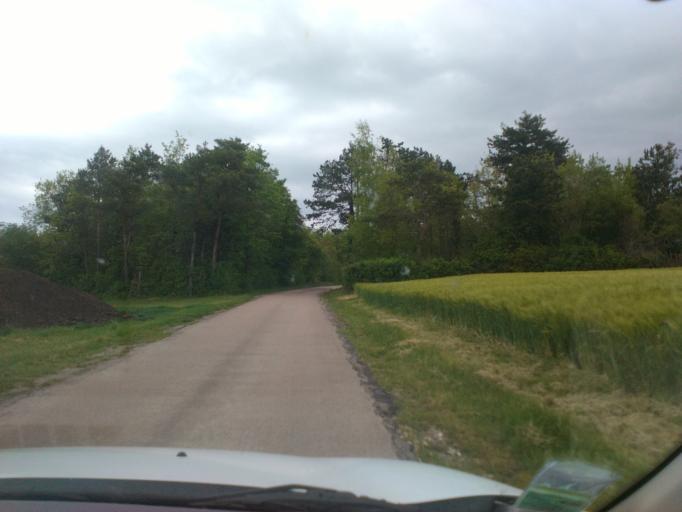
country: FR
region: Bourgogne
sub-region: Departement de l'Yonne
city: Thorigny-sur-Oreuse
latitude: 48.3709
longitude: 3.4644
